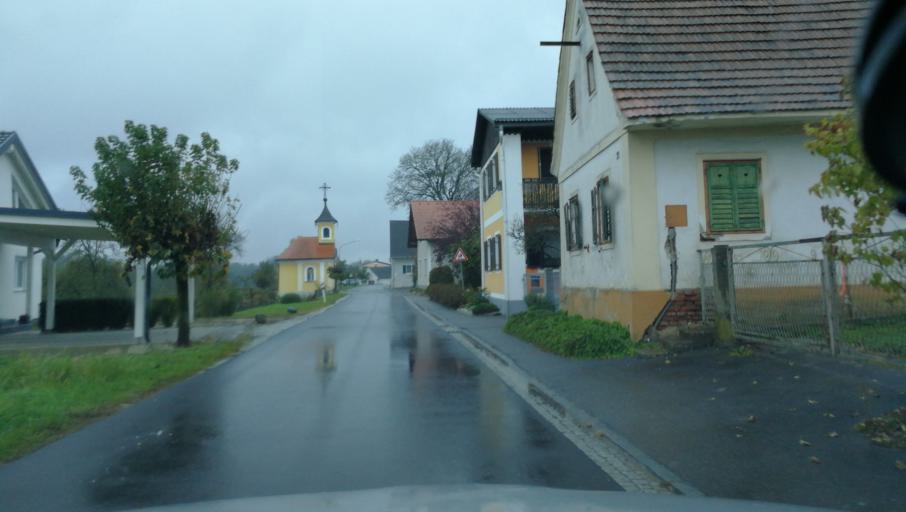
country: AT
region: Styria
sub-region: Politischer Bezirk Leibnitz
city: Strass in Steiermark
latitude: 46.7399
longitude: 15.6424
